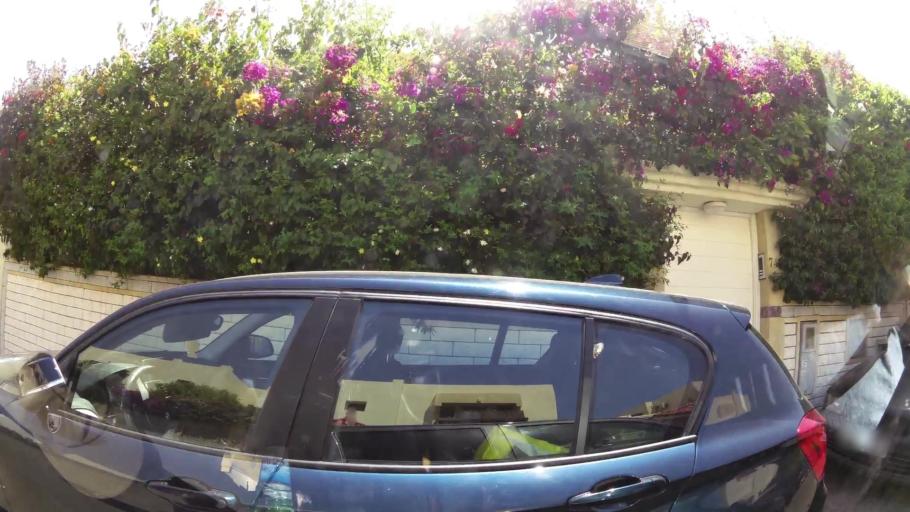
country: MA
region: Souss-Massa-Draa
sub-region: Agadir-Ida-ou-Tnan
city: Agadir
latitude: 30.4332
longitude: -9.5858
